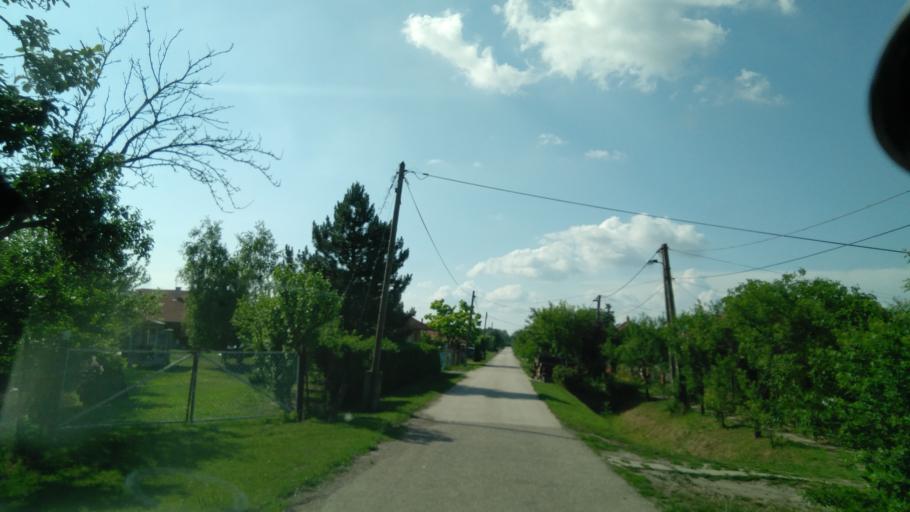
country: HU
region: Bekes
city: Doboz
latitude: 46.7011
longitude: 21.1794
